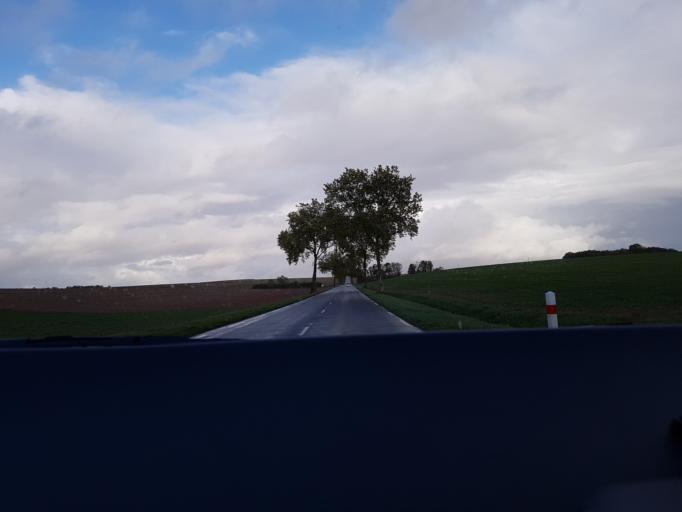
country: FR
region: Poitou-Charentes
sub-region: Departement de la Charente-Maritime
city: Aulnay
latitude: 46.0047
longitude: -0.3894
